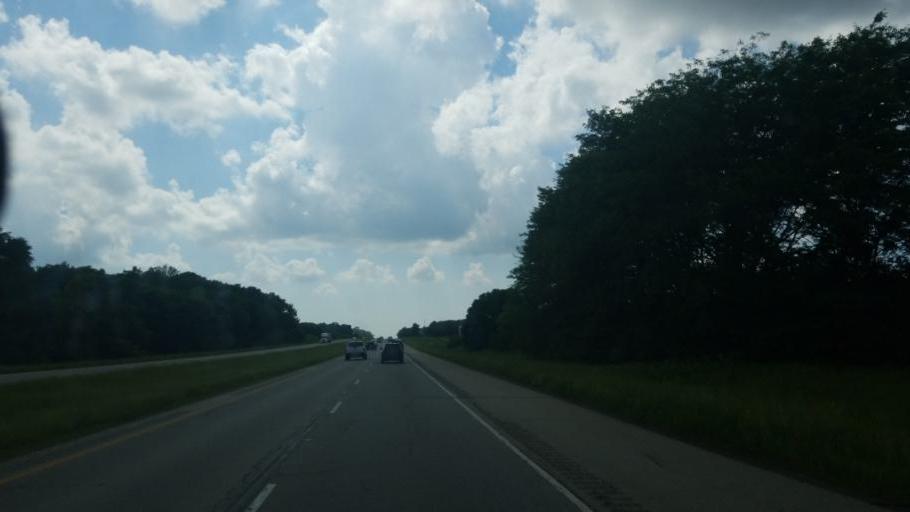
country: US
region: Indiana
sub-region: Kosciusko County
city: Warsaw
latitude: 41.2700
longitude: -85.8892
